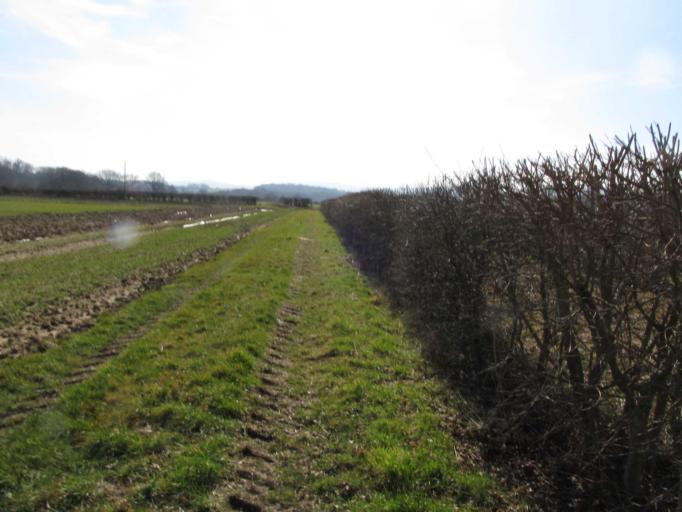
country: GB
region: England
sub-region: West Sussex
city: Petworth
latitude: 50.9688
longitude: -0.6047
